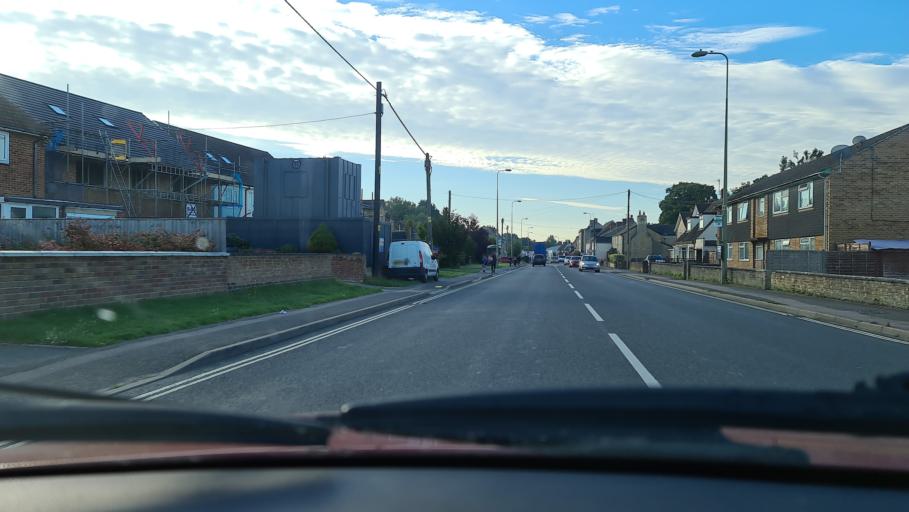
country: GB
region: England
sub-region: Oxfordshire
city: Kidlington
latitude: 51.8254
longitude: -1.2935
